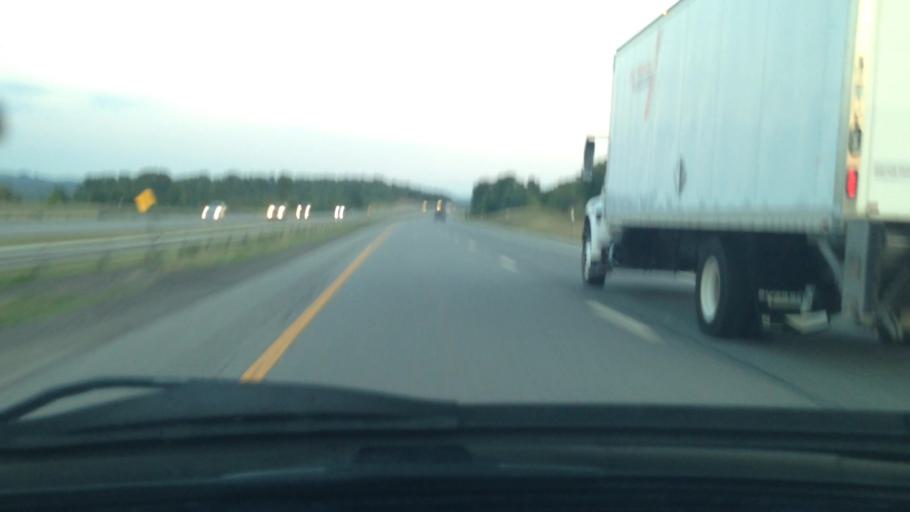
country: US
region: New York
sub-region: Montgomery County
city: Saint Johnsville
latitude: 42.9788
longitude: -74.6554
